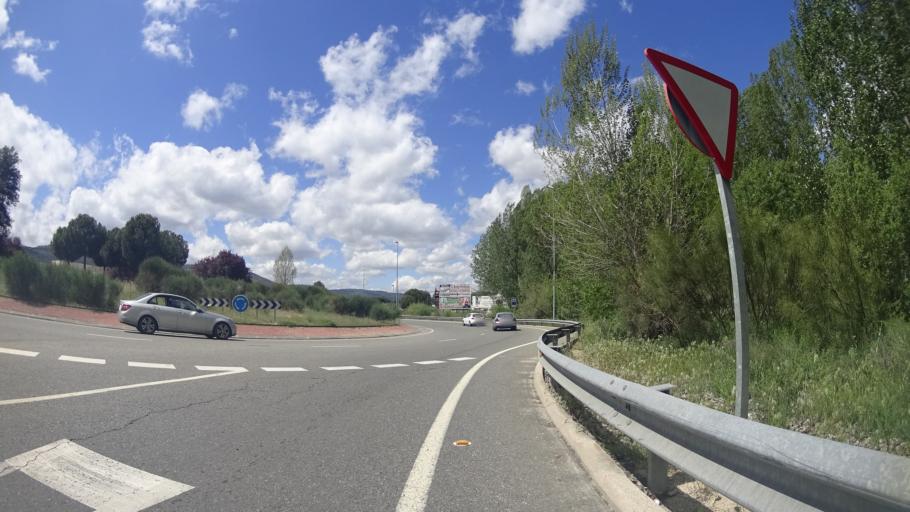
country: ES
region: Madrid
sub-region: Provincia de Madrid
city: Pelayos de la Presa
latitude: 40.3658
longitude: -4.3127
